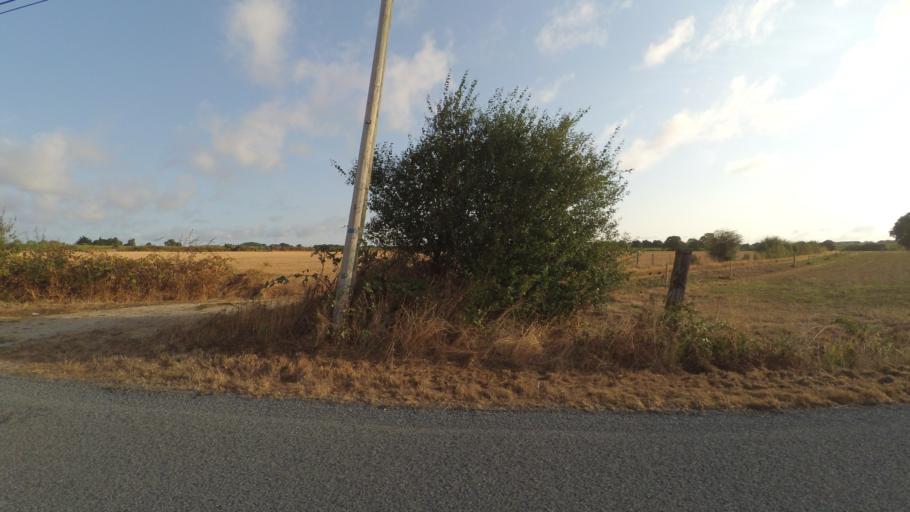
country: FR
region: Pays de la Loire
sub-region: Departement de la Loire-Atlantique
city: La Planche
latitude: 47.0185
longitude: -1.4187
